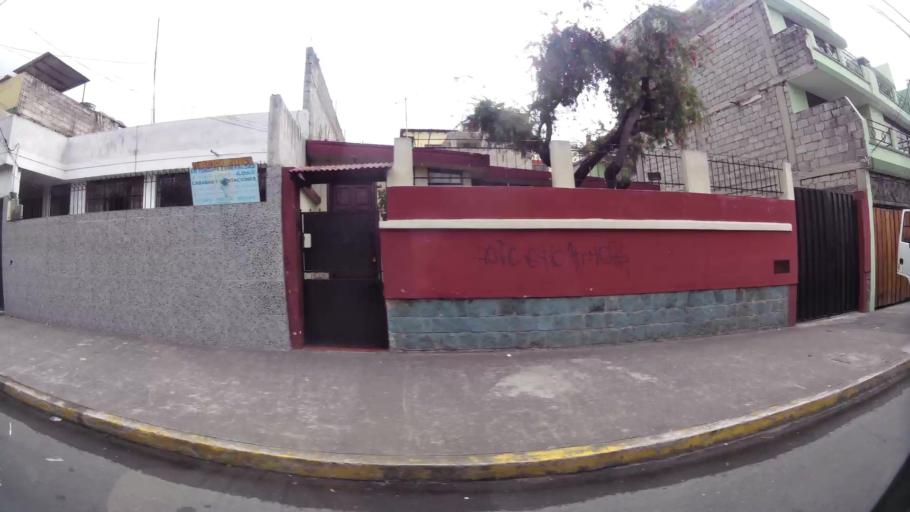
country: EC
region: Pichincha
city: Quito
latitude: -0.1427
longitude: -78.4964
